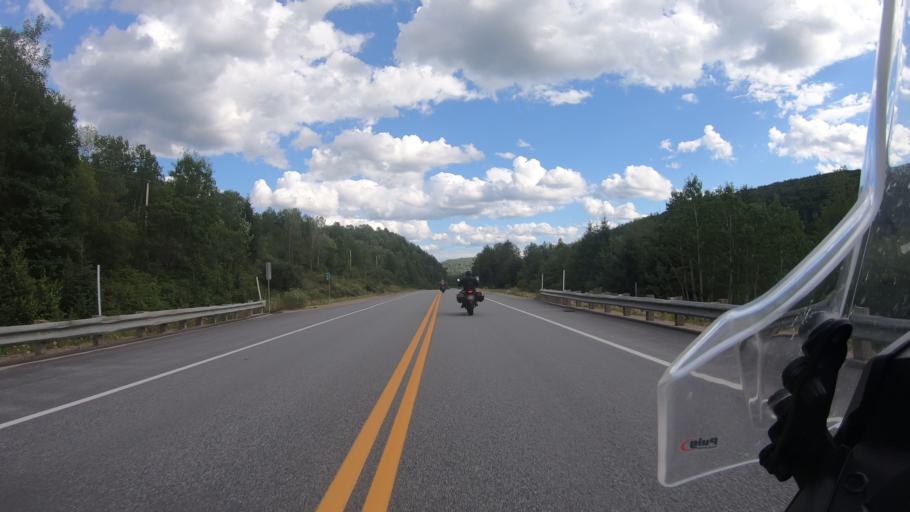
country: CA
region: Quebec
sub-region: Mauricie
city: Saint-Tite
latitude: 47.0043
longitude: -72.9262
